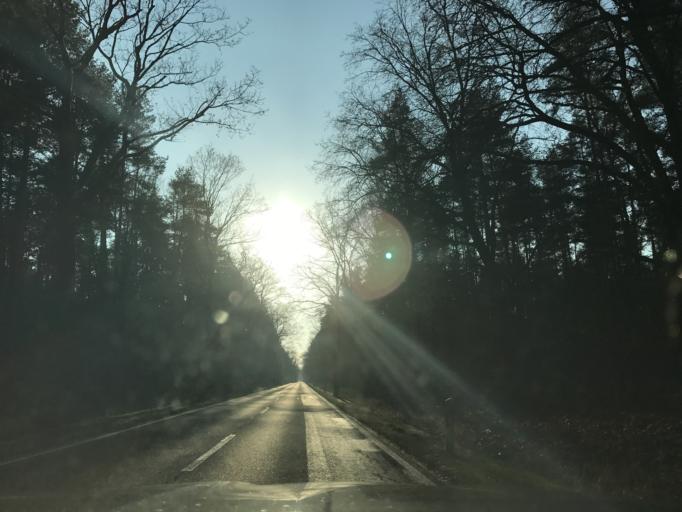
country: DE
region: Brandenburg
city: Wenzlow
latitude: 52.3459
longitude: 12.5001
